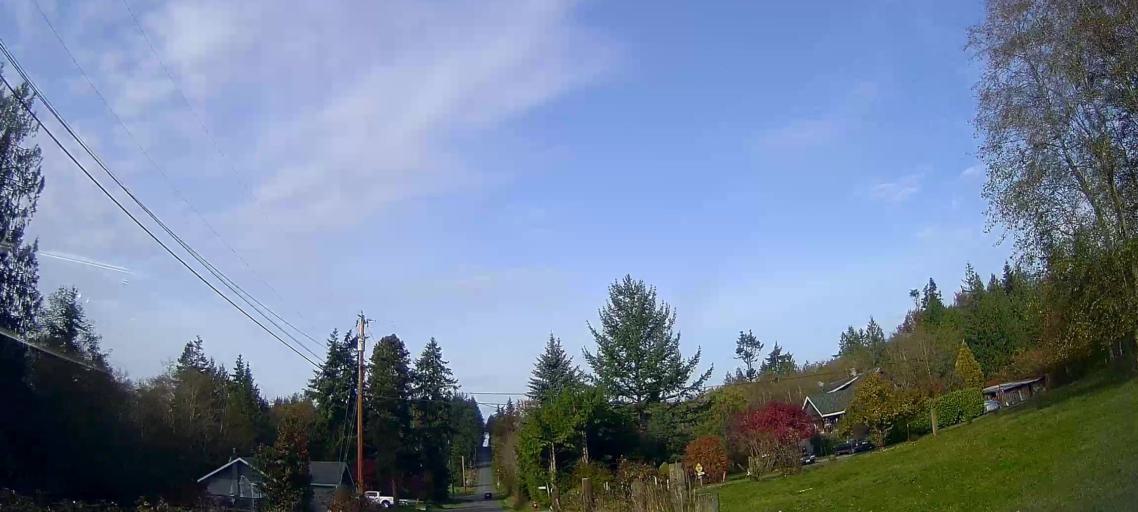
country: US
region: Washington
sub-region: Snohomish County
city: Stanwood
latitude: 48.2573
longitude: -122.3414
